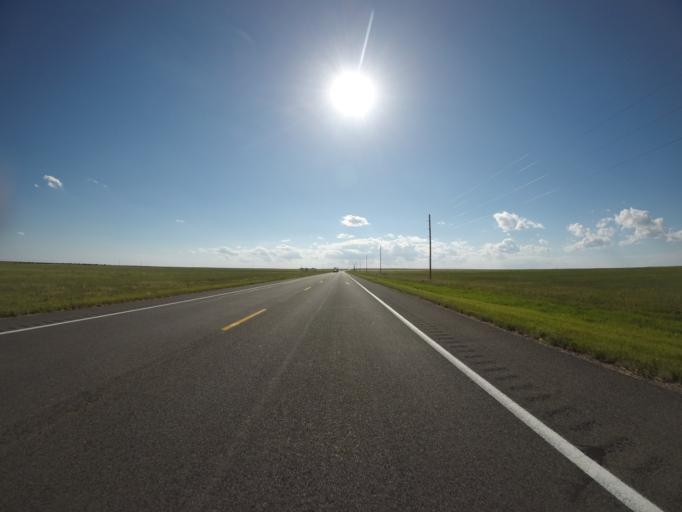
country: US
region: Colorado
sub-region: Morgan County
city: Brush
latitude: 40.6097
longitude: -103.6908
